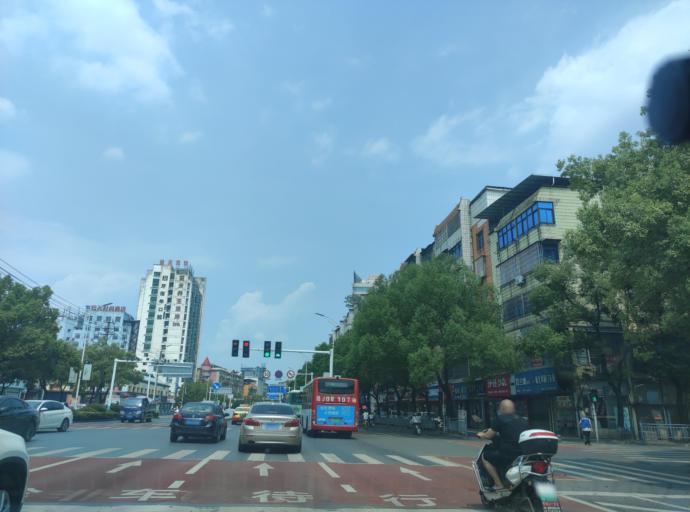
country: CN
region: Jiangxi Sheng
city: Pingxiang
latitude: 27.6409
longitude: 113.8616
